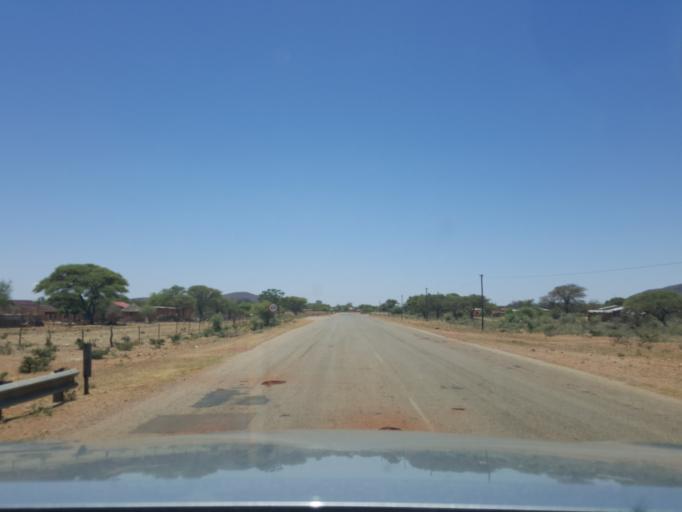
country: BW
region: South East
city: Ramotswa
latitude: -24.9831
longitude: 25.8964
